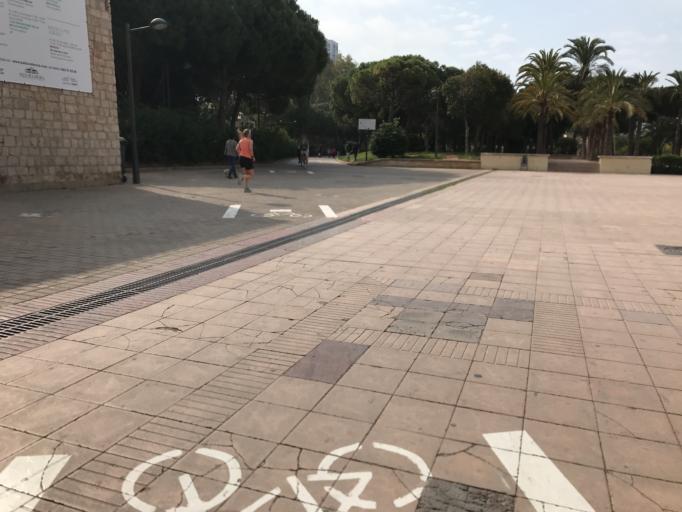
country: ES
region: Valencia
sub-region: Provincia de Valencia
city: Valencia
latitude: 39.4658
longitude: -0.3609
